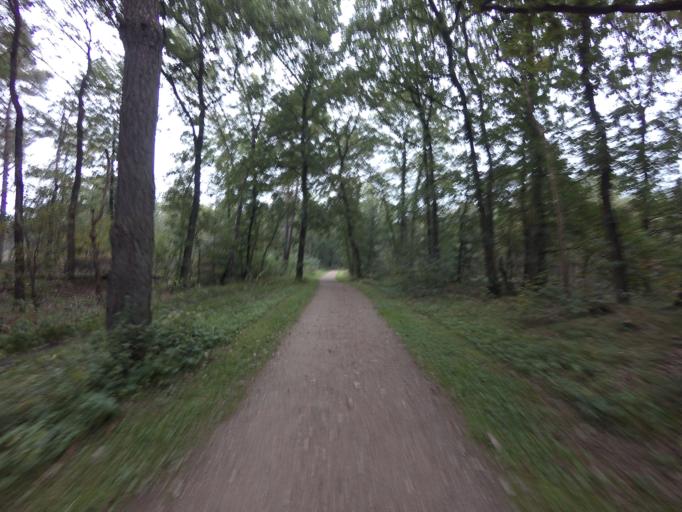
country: NL
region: North Holland
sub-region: Gemeente Hilversum
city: Hilversum
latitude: 52.2020
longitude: 5.2028
